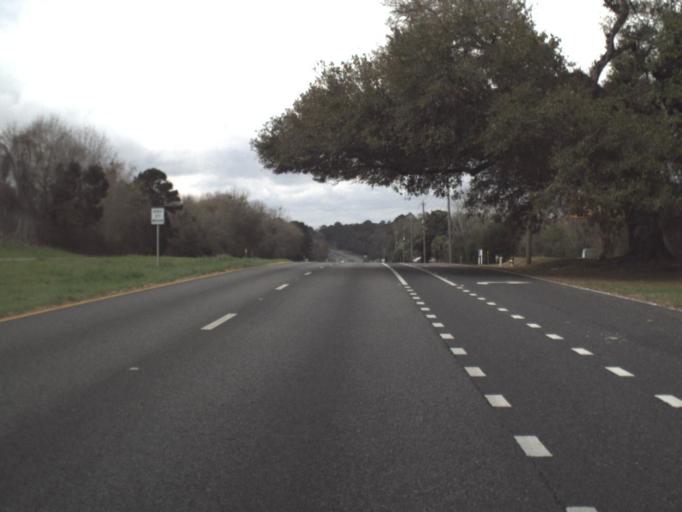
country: US
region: Florida
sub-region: Leon County
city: Tallahassee
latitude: 30.4267
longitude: -84.1847
